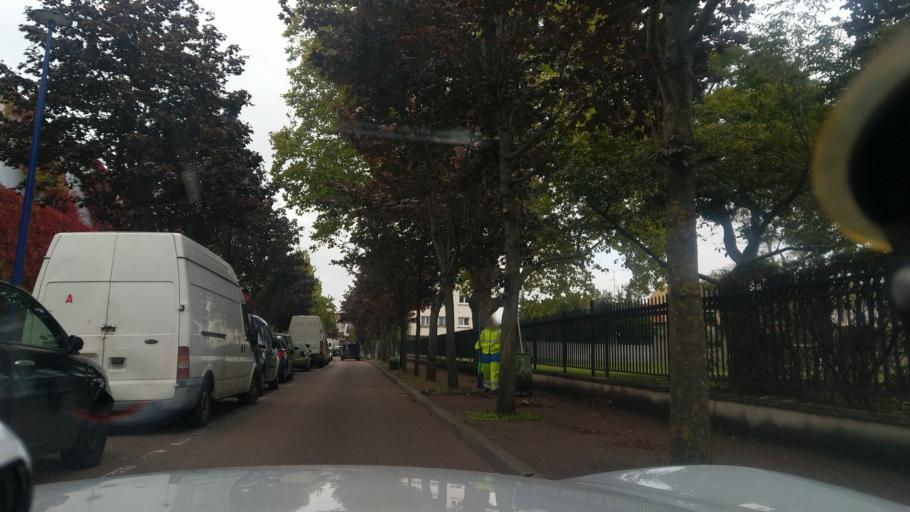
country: FR
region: Ile-de-France
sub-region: Departement de Seine-Saint-Denis
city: Le Bourget
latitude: 48.9216
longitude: 2.4280
